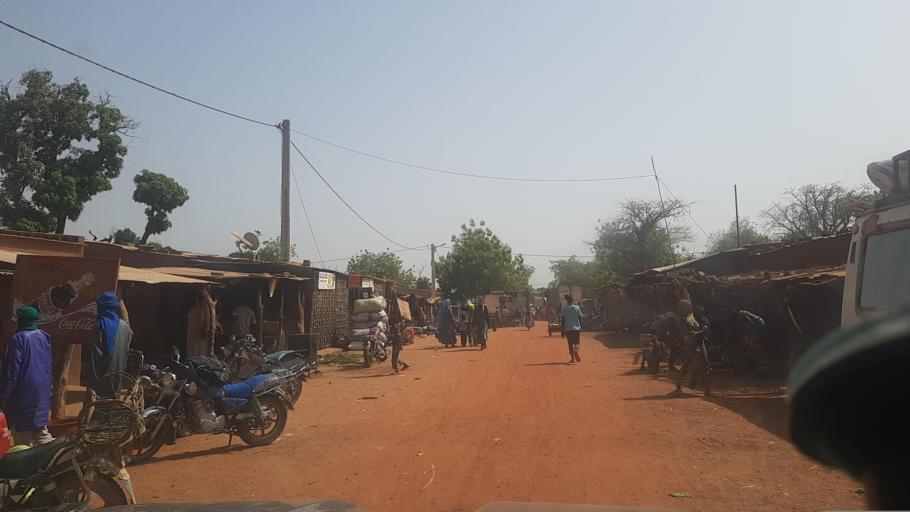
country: ML
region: Segou
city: Baroueli
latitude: 12.9493
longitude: -6.3776
